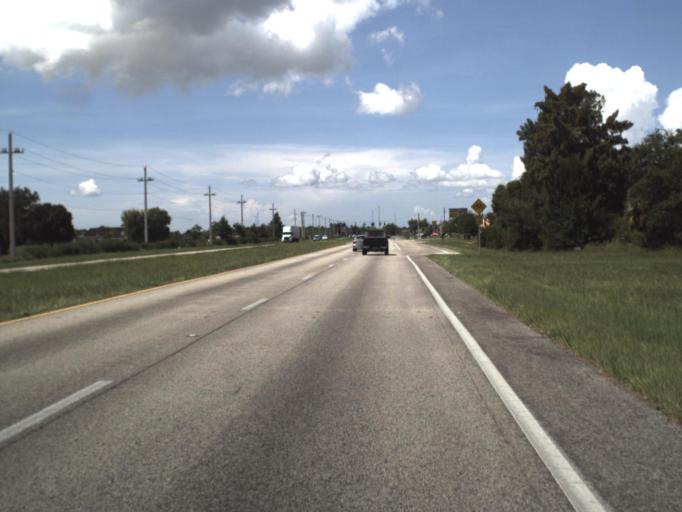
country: US
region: Florida
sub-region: Charlotte County
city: Cleveland
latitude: 26.9453
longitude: -82.0064
